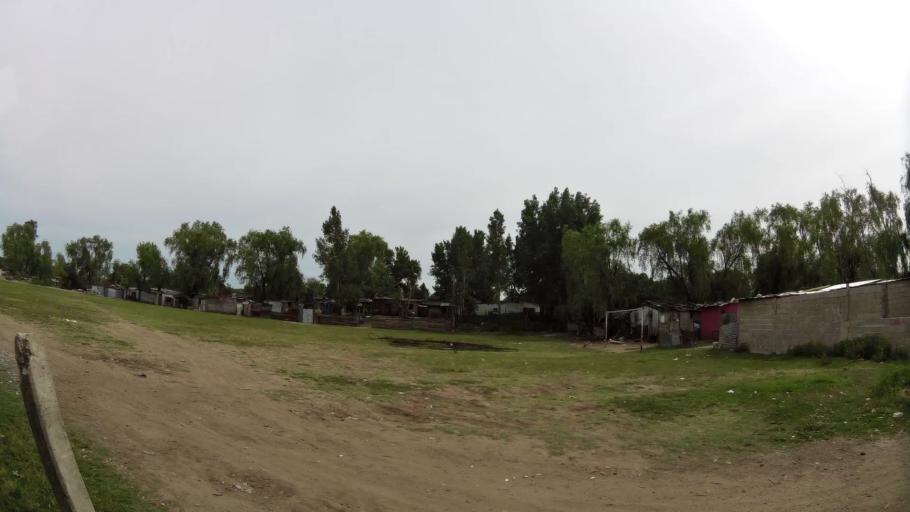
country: UY
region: Montevideo
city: Montevideo
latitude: -34.8348
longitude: -56.1767
